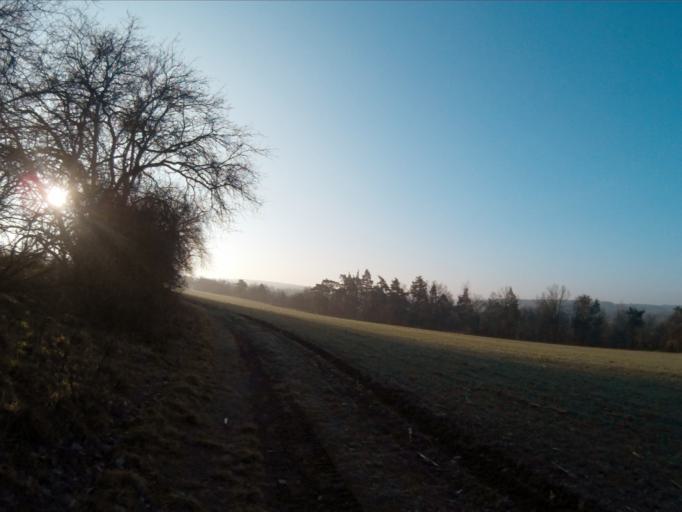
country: CZ
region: Vysocina
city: Namest' nad Oslavou
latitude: 49.1992
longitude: 16.1602
